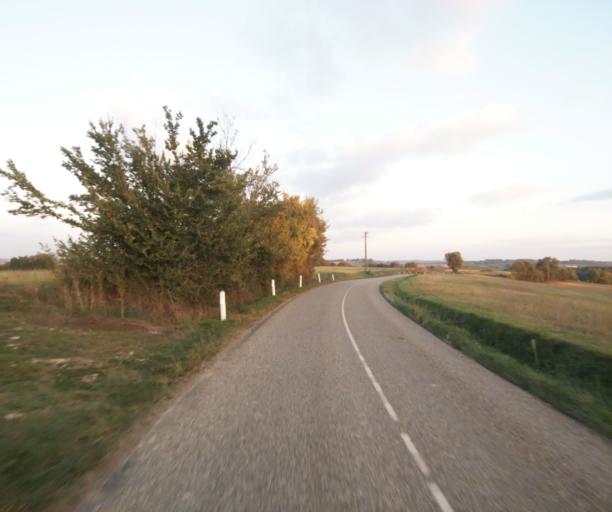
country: FR
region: Midi-Pyrenees
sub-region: Departement du Gers
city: Vic-Fezensac
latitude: 43.7971
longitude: 0.2445
